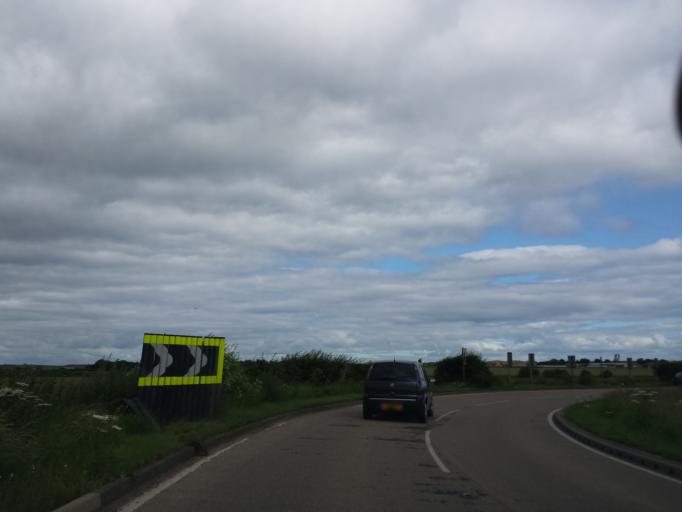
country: GB
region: Scotland
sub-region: East Lothian
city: Gullane
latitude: 56.0123
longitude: -2.7880
